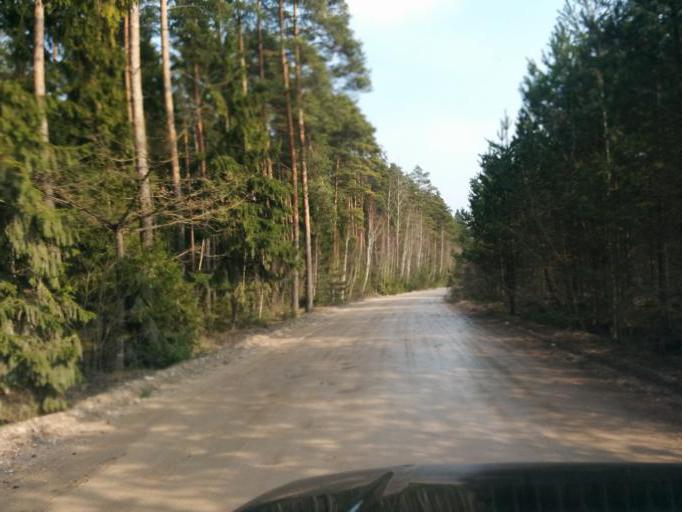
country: LV
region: Olaine
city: Olaine
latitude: 56.7914
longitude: 24.0214
